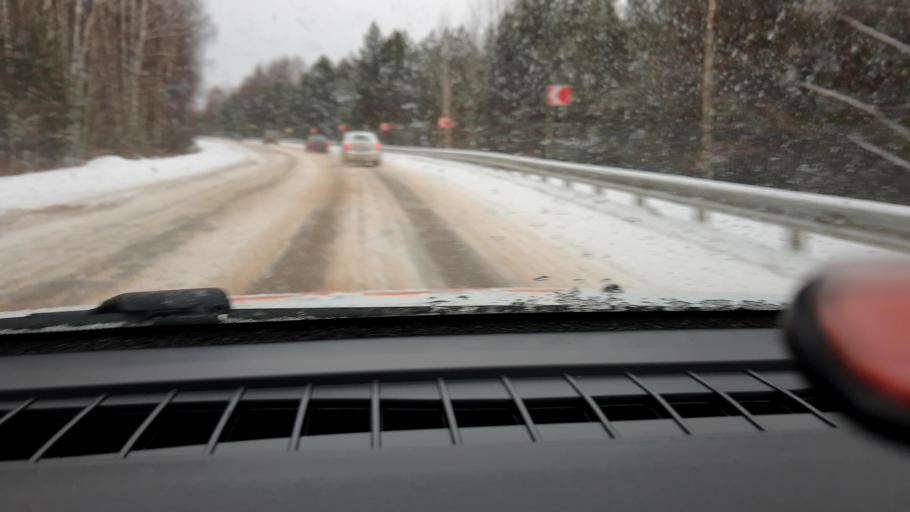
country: RU
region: Nizjnij Novgorod
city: Kstovo
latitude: 56.2815
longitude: 44.3163
